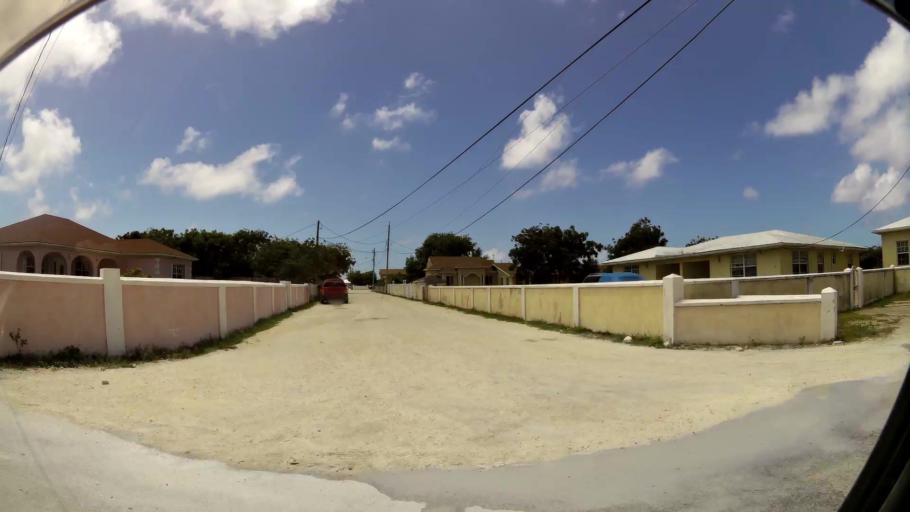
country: TC
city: Cockburn Town
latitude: 21.4598
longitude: -71.1392
